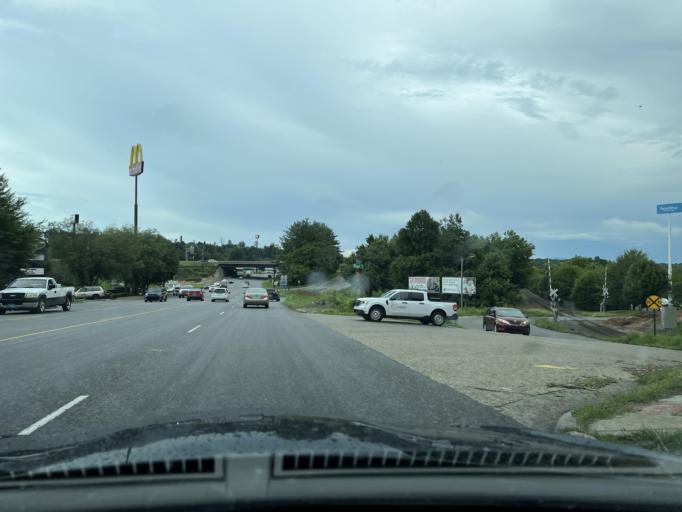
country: US
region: North Carolina
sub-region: Buncombe County
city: Bent Creek
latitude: 35.5568
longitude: -82.6403
